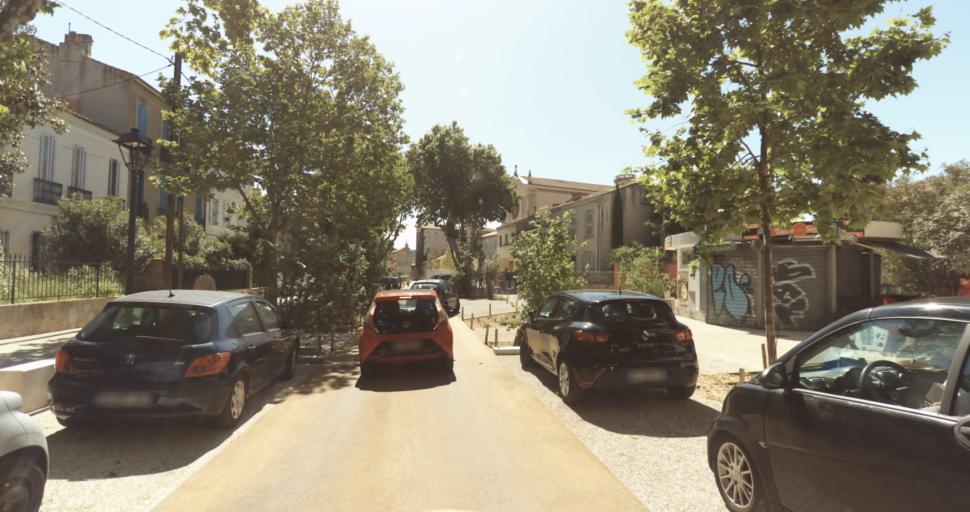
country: FR
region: Provence-Alpes-Cote d'Azur
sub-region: Departement du Var
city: La Seyne-sur-Mer
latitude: 43.1022
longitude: 5.8756
